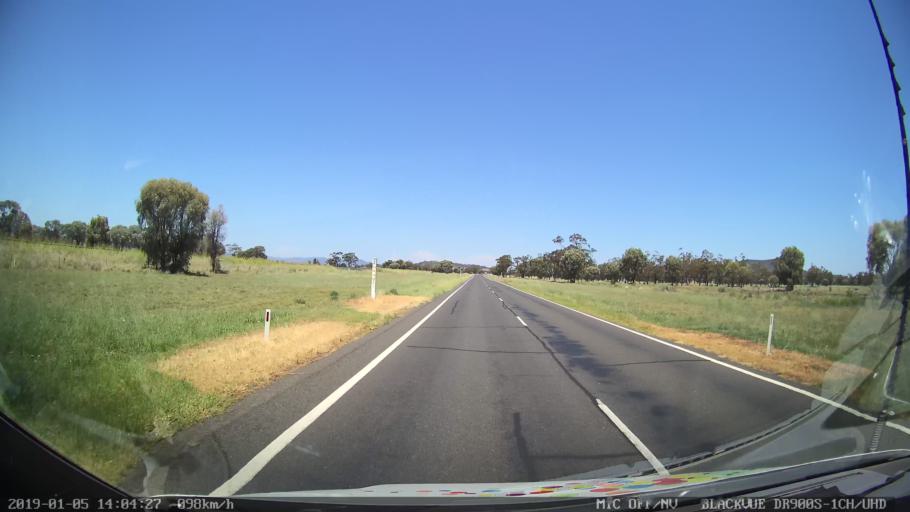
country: AU
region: New South Wales
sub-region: Gunnedah
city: Gunnedah
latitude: -31.2001
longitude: 150.3640
